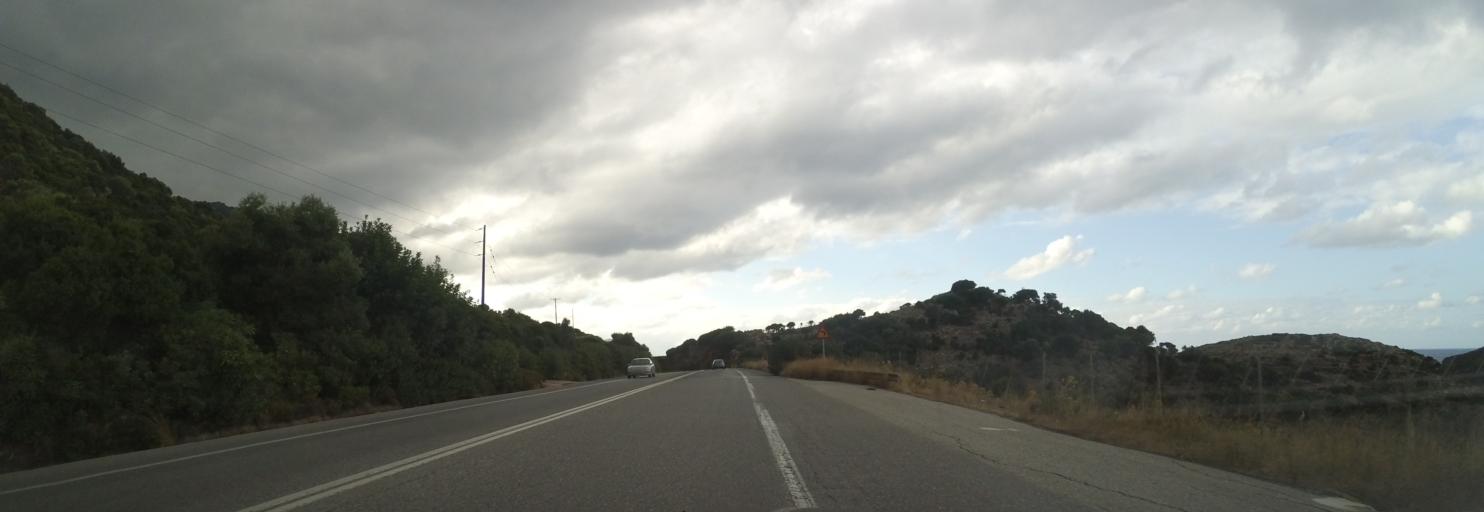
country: GR
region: Crete
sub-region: Nomos Rethymnis
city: Zoniana
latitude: 35.4082
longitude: 24.8263
